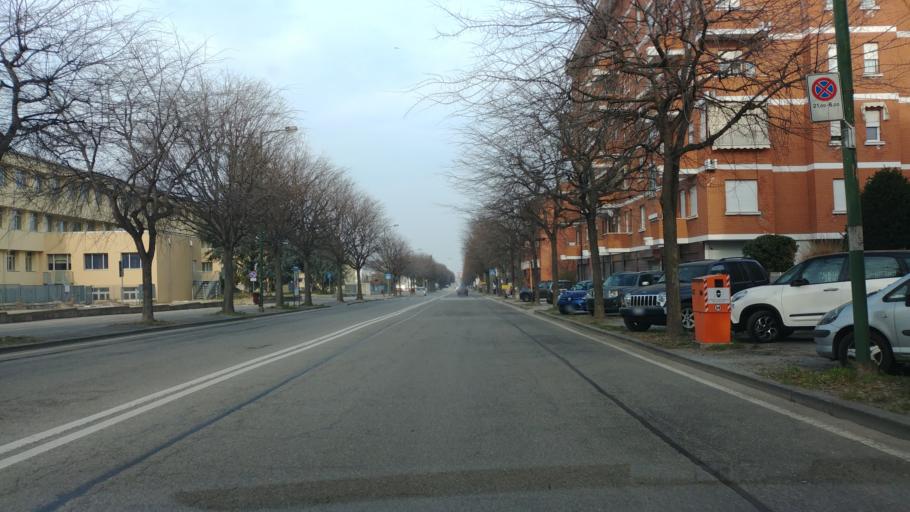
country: IT
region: Piedmont
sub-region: Provincia di Cuneo
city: Cuneo
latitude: 44.3774
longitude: 7.5272
